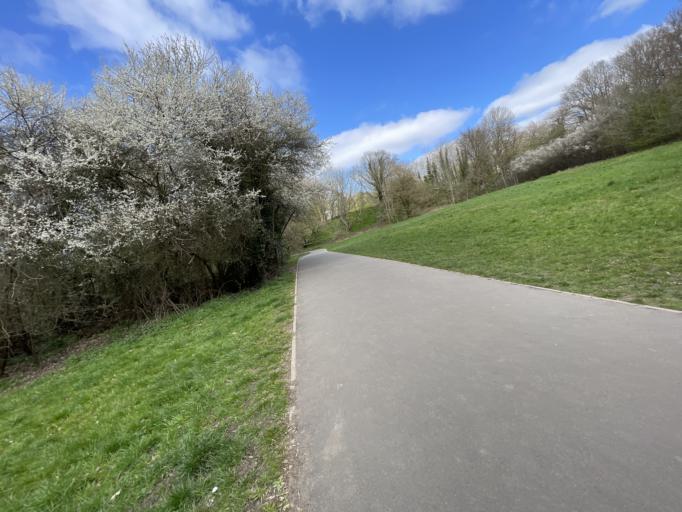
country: GB
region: England
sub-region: Greater London
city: Barnet
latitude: 51.6285
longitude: -0.1814
